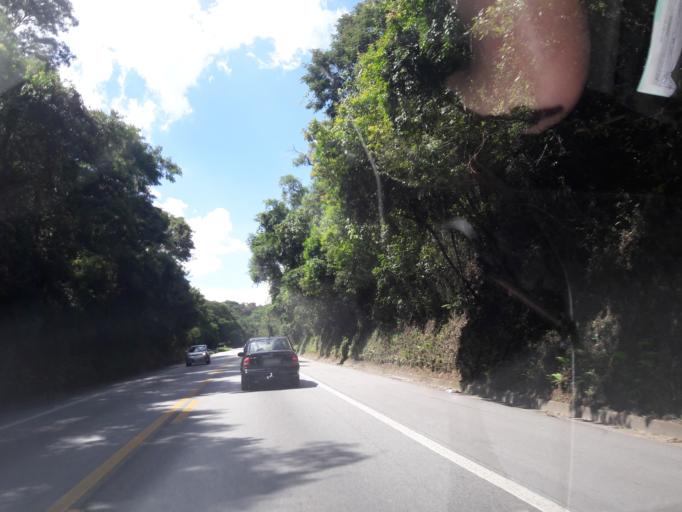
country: BR
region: Sao Paulo
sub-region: Francisco Morato
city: Francisco Morato
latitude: -23.3002
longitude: -46.8093
